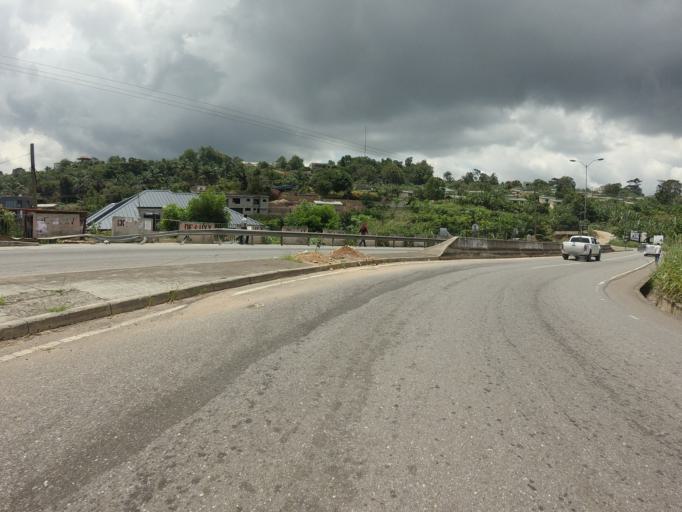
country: GH
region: Eastern
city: Aburi
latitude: 5.8014
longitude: -0.1826
